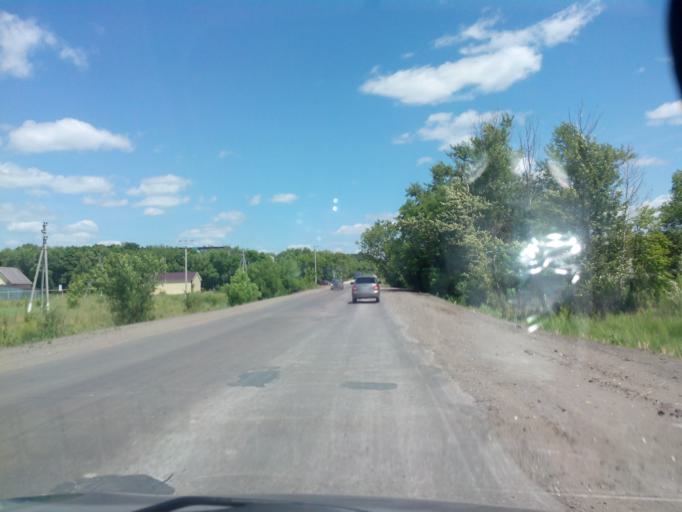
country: RU
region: Tambov
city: Zherdevka
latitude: 51.8151
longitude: 41.5099
